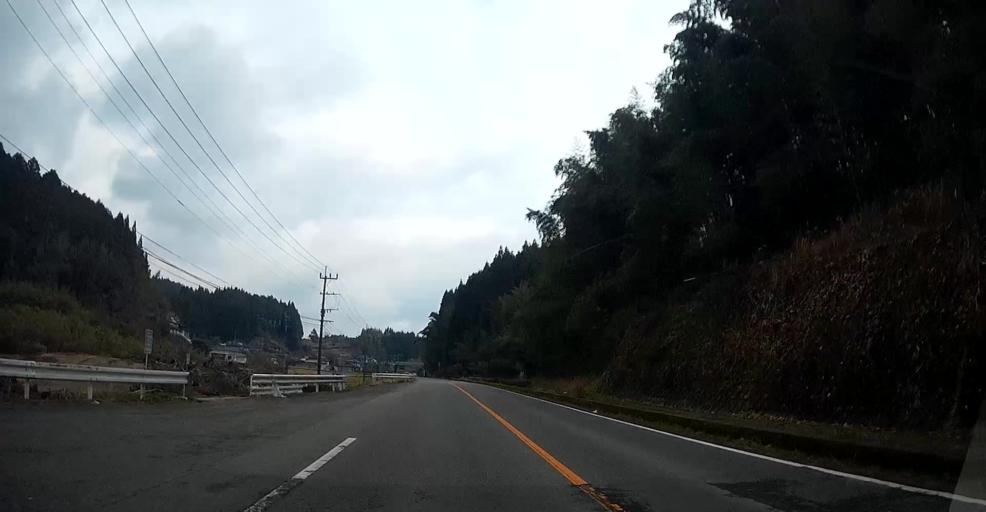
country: JP
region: Kumamoto
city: Matsubase
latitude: 32.6207
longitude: 130.8627
